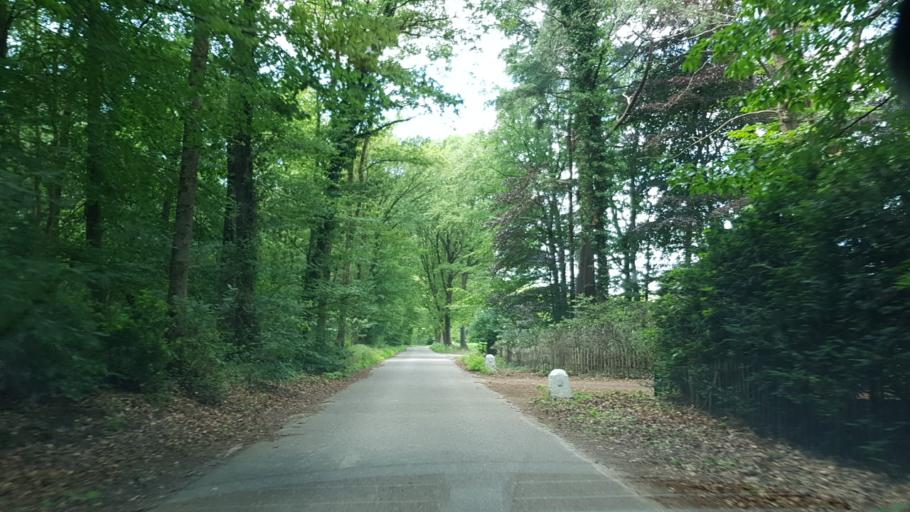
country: NL
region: Gelderland
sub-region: Gemeente Ede
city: Lunteren
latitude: 52.0939
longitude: 5.6373
